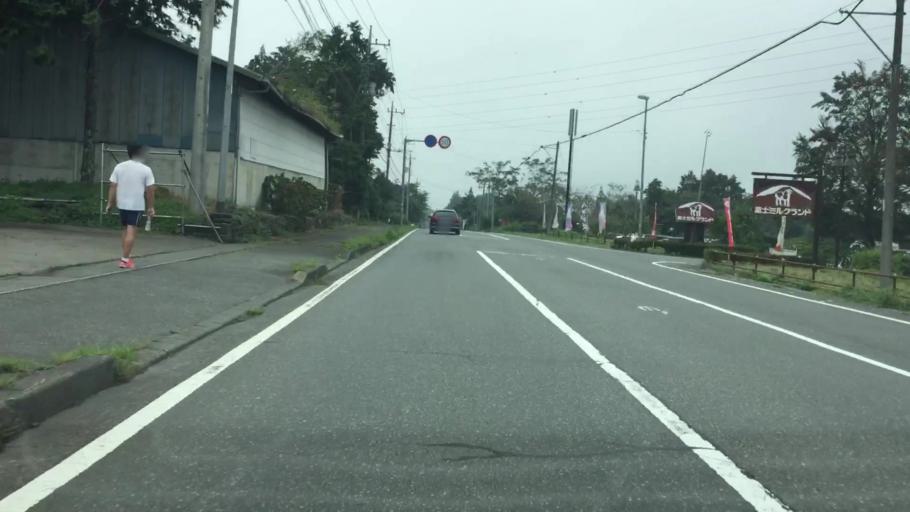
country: JP
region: Shizuoka
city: Fujinomiya
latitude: 35.3406
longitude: 138.5950
